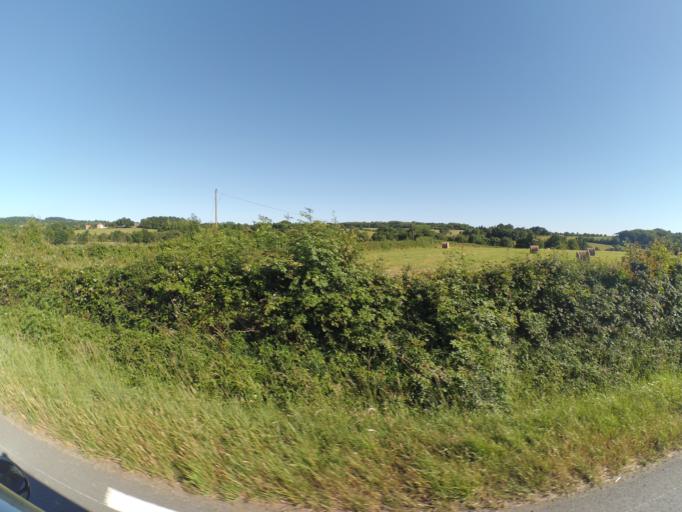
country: FR
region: Pays de la Loire
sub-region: Departement de la Vendee
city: Saint-Paul-en-Pareds
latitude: 46.8507
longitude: -0.9479
